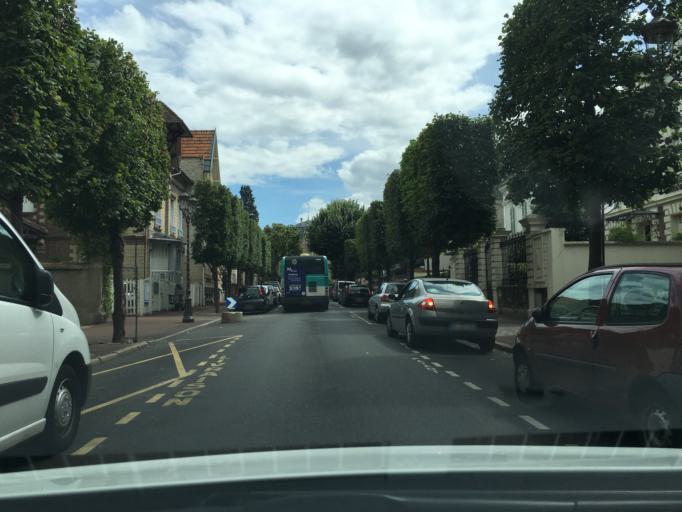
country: FR
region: Ile-de-France
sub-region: Departement des Hauts-de-Seine
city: Rueil-Malmaison
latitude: 48.8792
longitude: 2.1797
